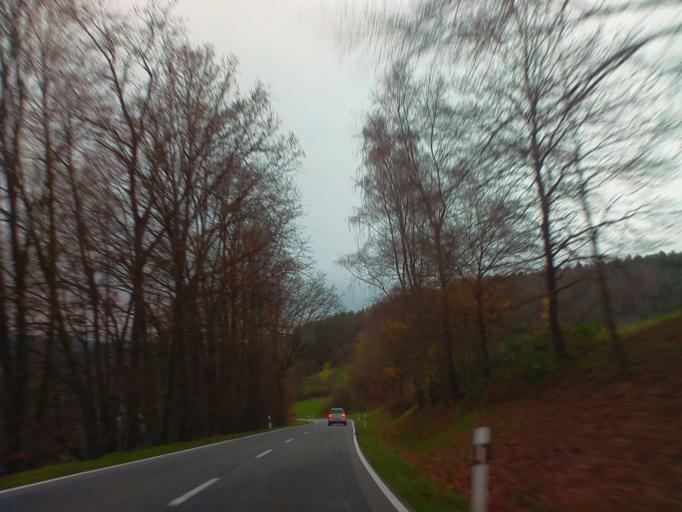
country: DE
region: Hesse
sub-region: Regierungsbezirk Darmstadt
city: Wald-Michelbach
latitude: 49.5963
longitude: 8.8964
